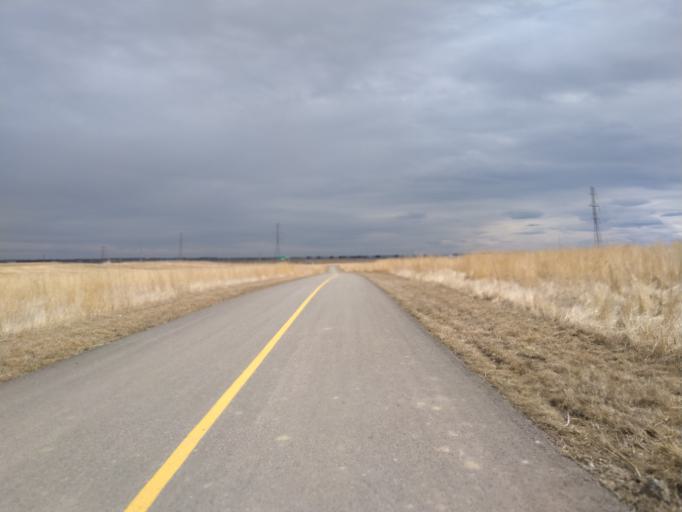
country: CA
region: Alberta
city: Airdrie
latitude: 51.1790
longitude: -114.0327
